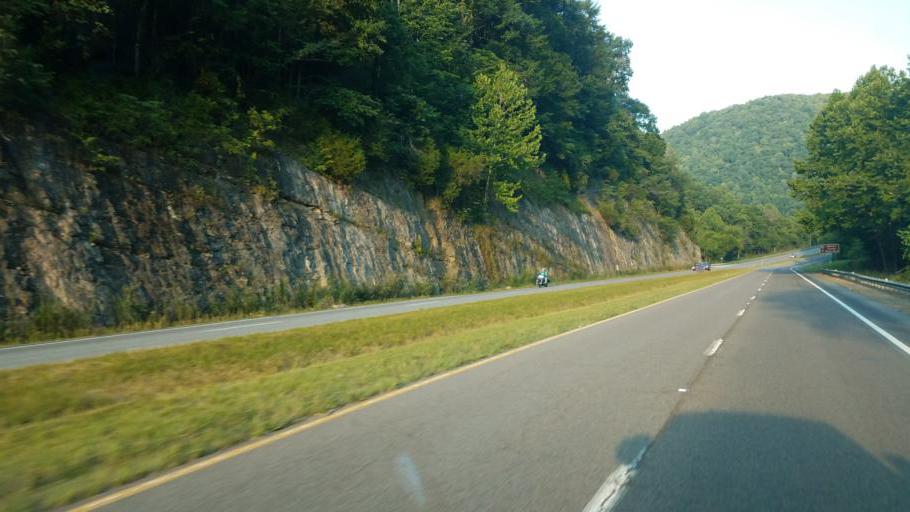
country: US
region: Tennessee
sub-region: Hawkins County
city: Mount Carmel
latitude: 36.6977
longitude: -82.7592
